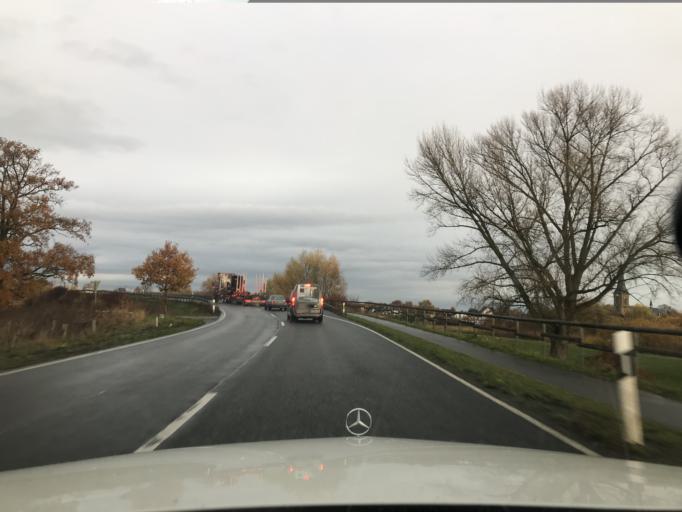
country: DE
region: North Rhine-Westphalia
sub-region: Regierungsbezirk Arnsberg
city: Welver
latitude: 51.6611
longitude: 8.0344
